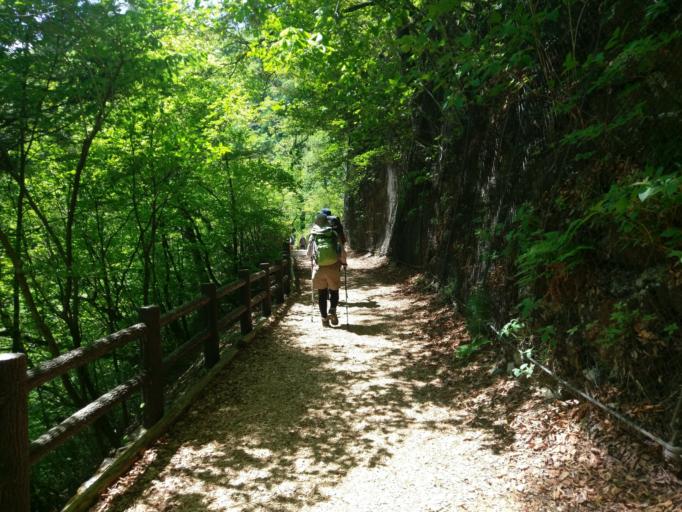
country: JP
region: Yamanashi
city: Uenohara
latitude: 35.7356
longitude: 139.0266
